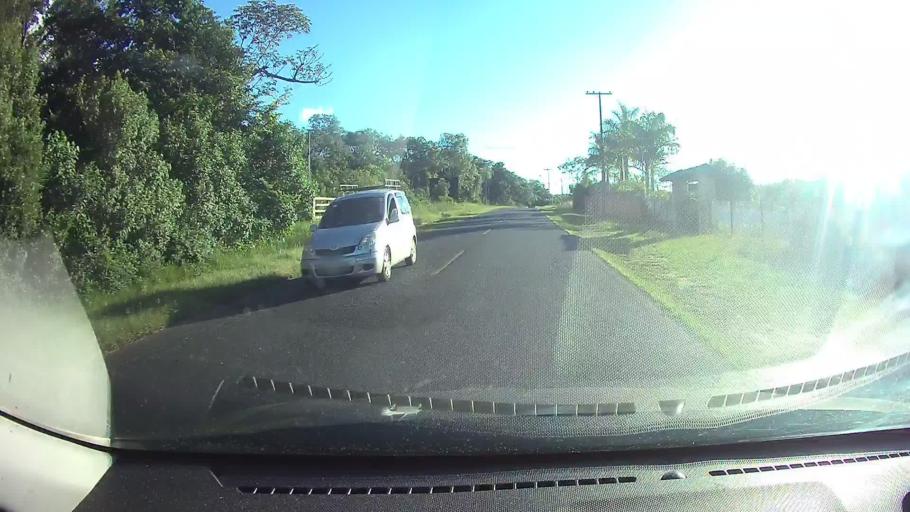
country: PY
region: Cordillera
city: Emboscada
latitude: -25.1834
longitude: -57.2971
